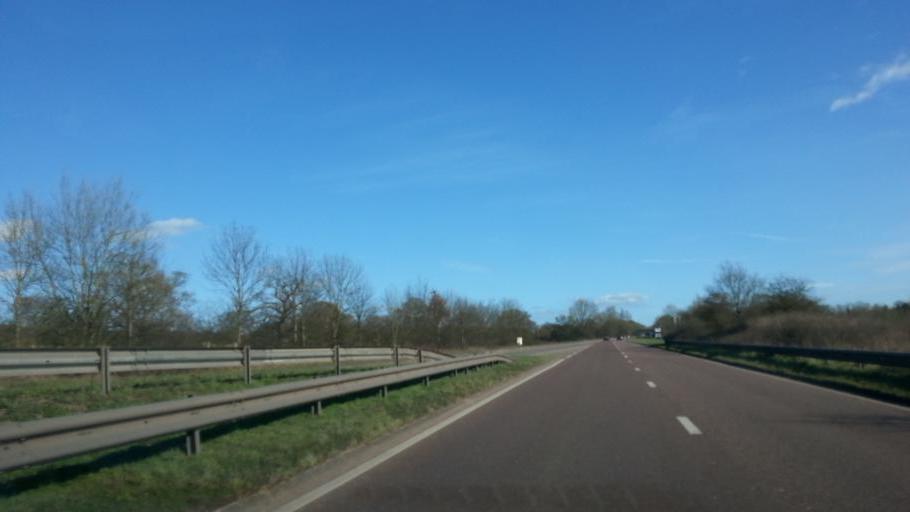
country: GB
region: England
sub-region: Solihull
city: Meriden
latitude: 52.4430
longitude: -1.6496
